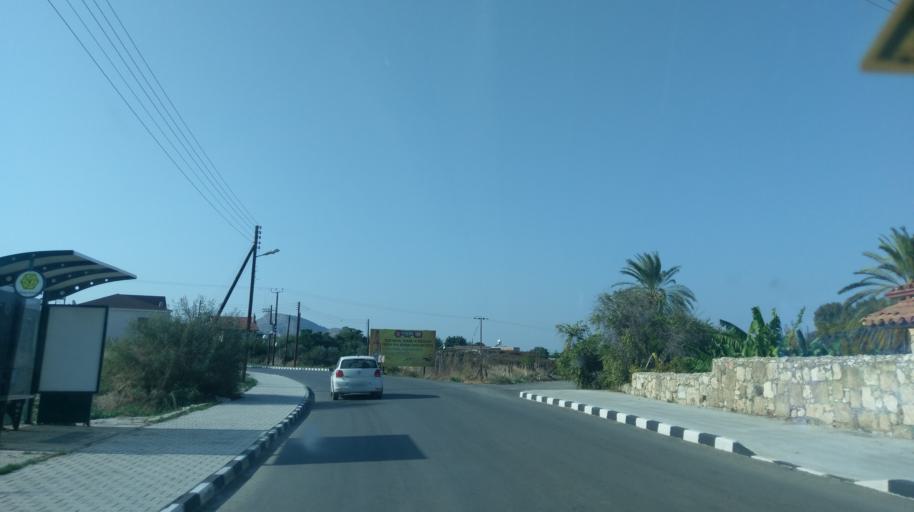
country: CY
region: Lefkosia
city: Lefka
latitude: 35.1422
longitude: 32.8139
